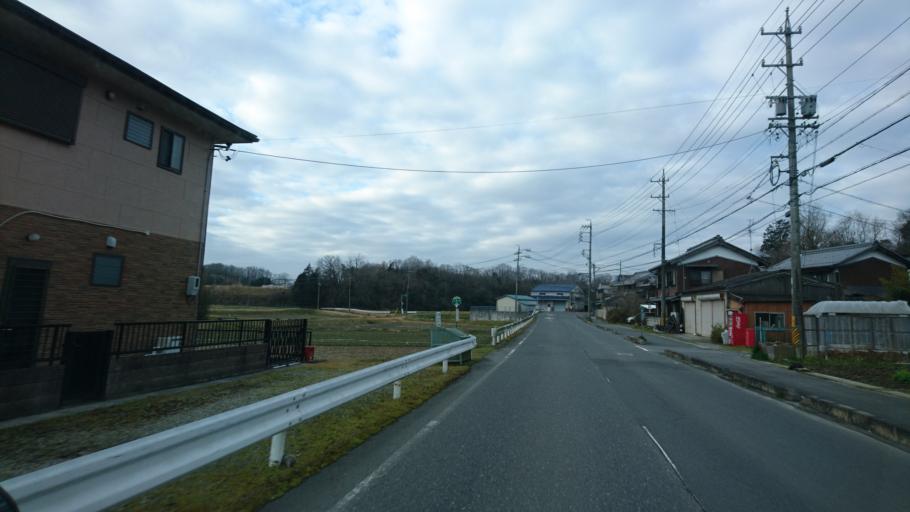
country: JP
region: Mie
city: Ueno-ebisumachi
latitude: 34.7322
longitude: 136.0950
